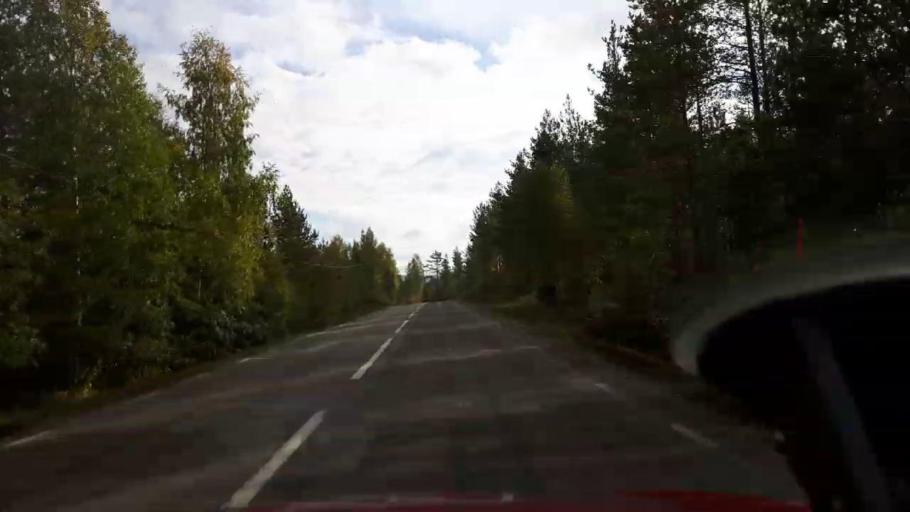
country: SE
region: Jaemtland
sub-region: Harjedalens Kommun
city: Sveg
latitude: 62.1235
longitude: 15.0069
